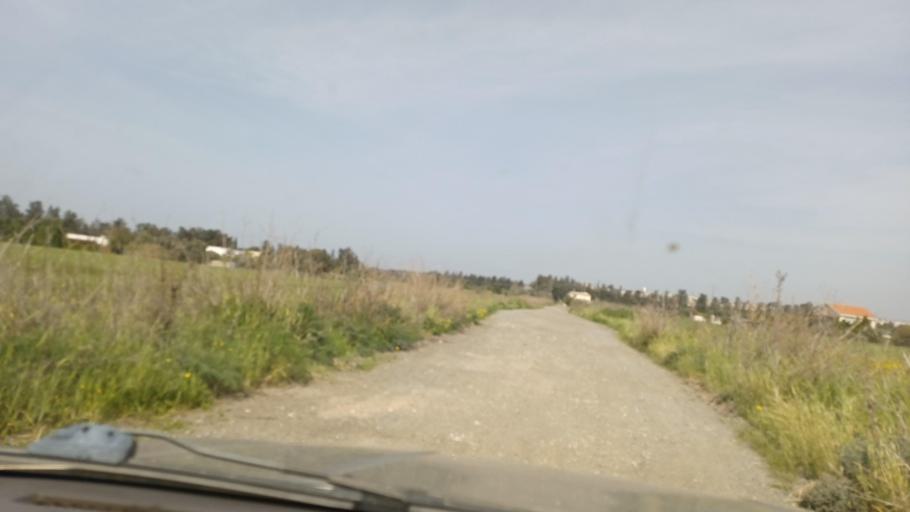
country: CY
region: Pafos
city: Paphos
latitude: 34.7437
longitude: 32.4634
